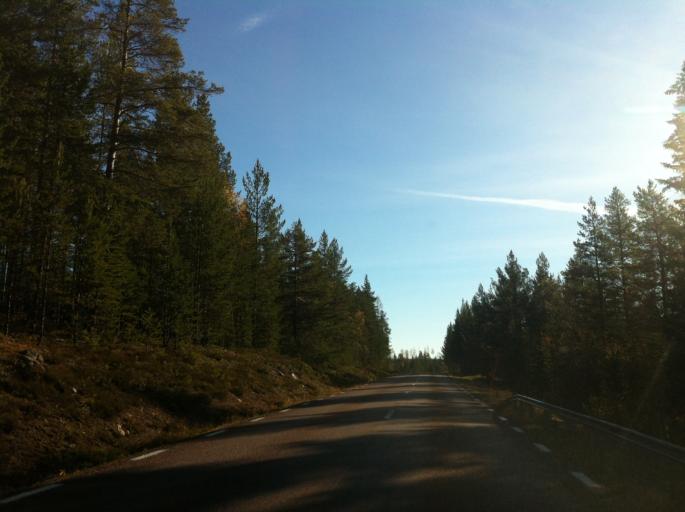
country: NO
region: Hedmark
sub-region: Trysil
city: Innbygda
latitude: 61.8221
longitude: 12.8892
